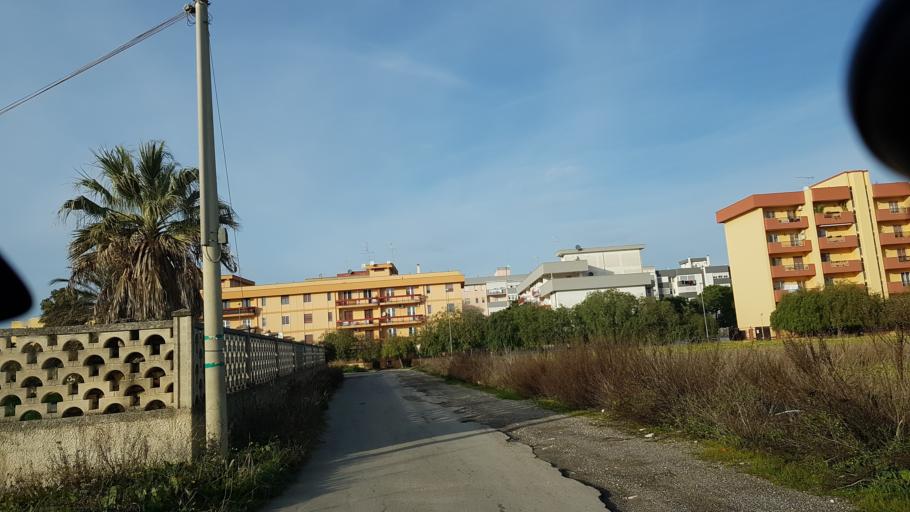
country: IT
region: Apulia
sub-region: Provincia di Brindisi
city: Brindisi
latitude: 40.6154
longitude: 17.9239
